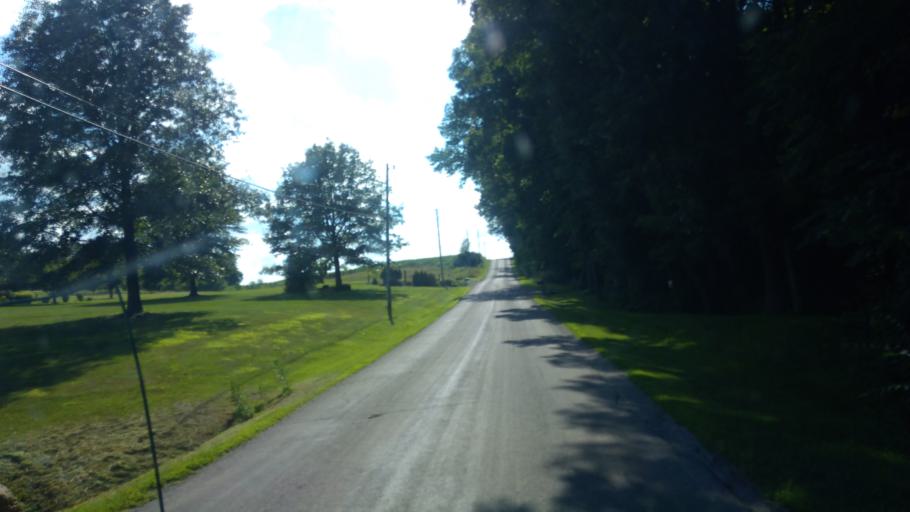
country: US
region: Ohio
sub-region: Wayne County
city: Dalton
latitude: 40.7556
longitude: -81.7112
